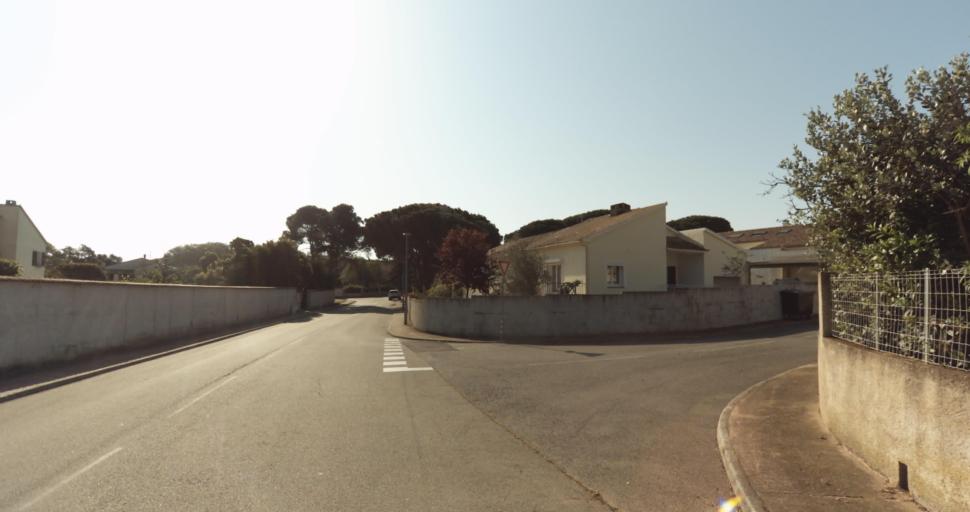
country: FR
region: Corsica
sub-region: Departement de la Haute-Corse
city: Biguglia
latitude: 42.6368
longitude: 9.4320
